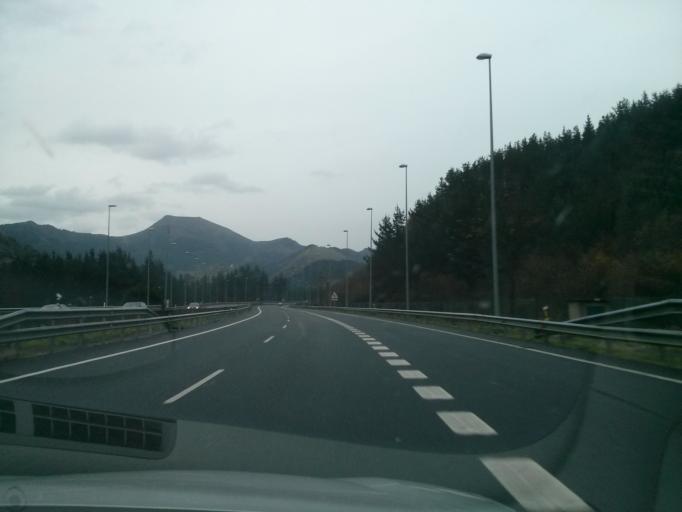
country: ES
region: Basque Country
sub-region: Bizkaia
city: Gordexola
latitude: 43.1978
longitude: -3.0777
